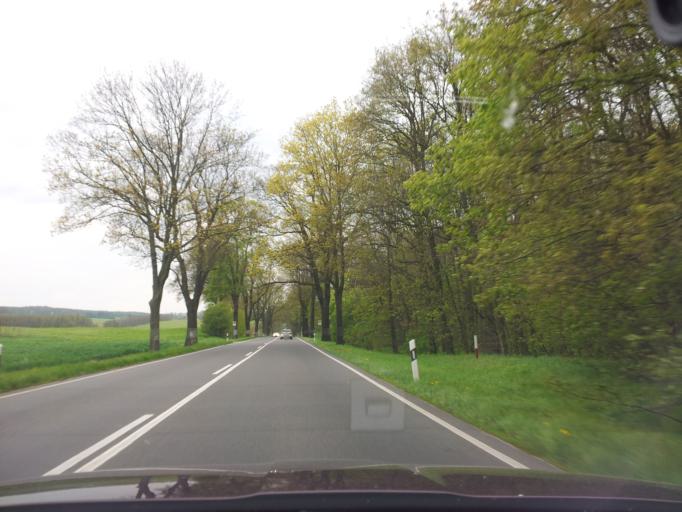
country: DE
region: Brandenburg
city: Lietzen
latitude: 52.5092
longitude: 14.2604
